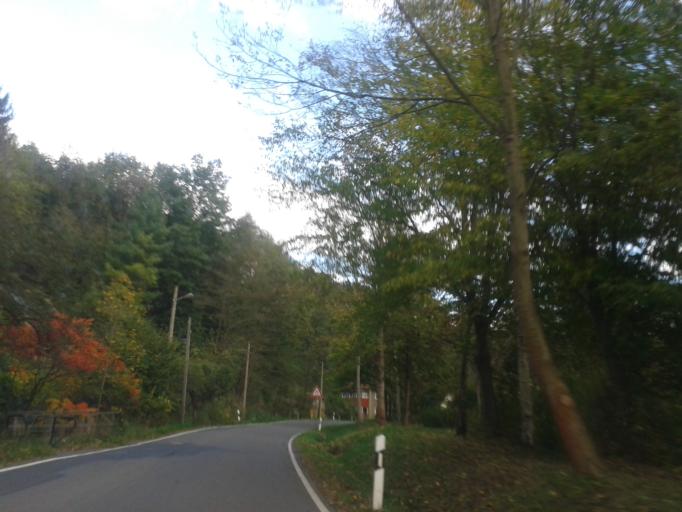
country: DE
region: Saxony
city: Reinsberg
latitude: 51.0079
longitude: 13.3701
